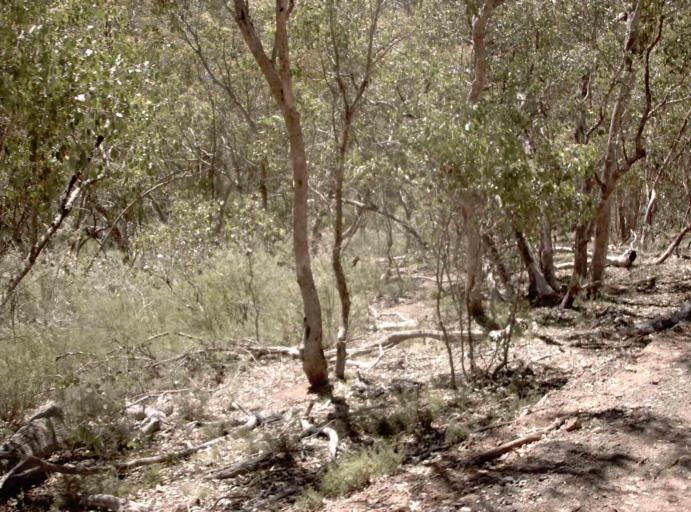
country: AU
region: New South Wales
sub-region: Snowy River
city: Jindabyne
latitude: -37.0763
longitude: 148.4617
